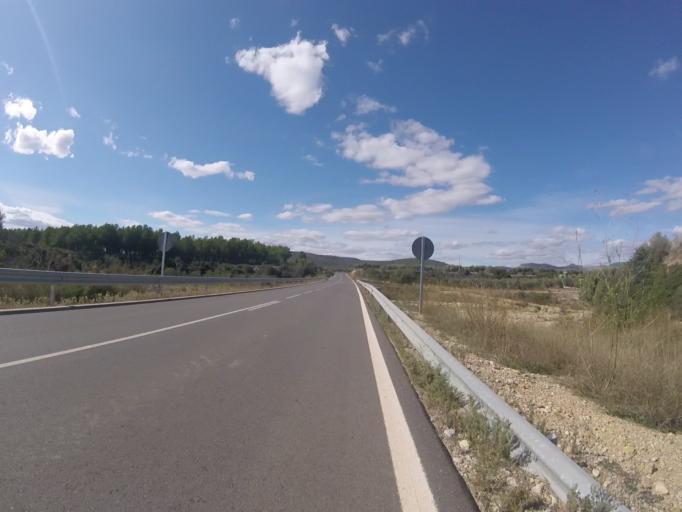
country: ES
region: Valencia
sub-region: Provincia de Castello
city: Chert/Xert
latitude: 40.4270
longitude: 0.1527
